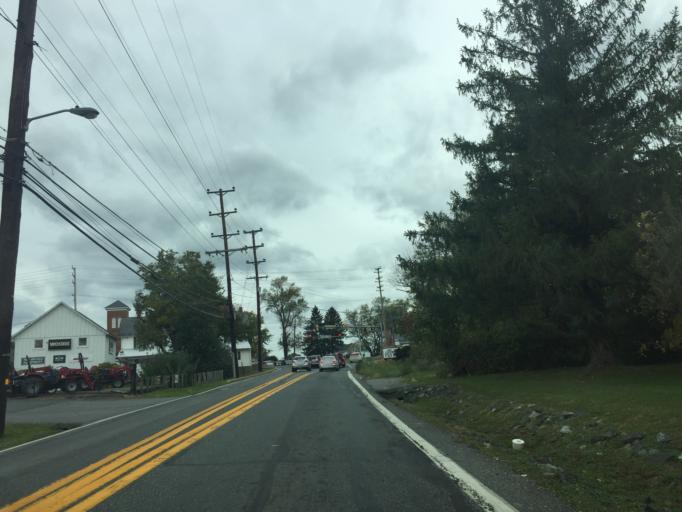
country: US
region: Maryland
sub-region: Harford County
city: Riverside
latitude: 39.5581
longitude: -76.2522
